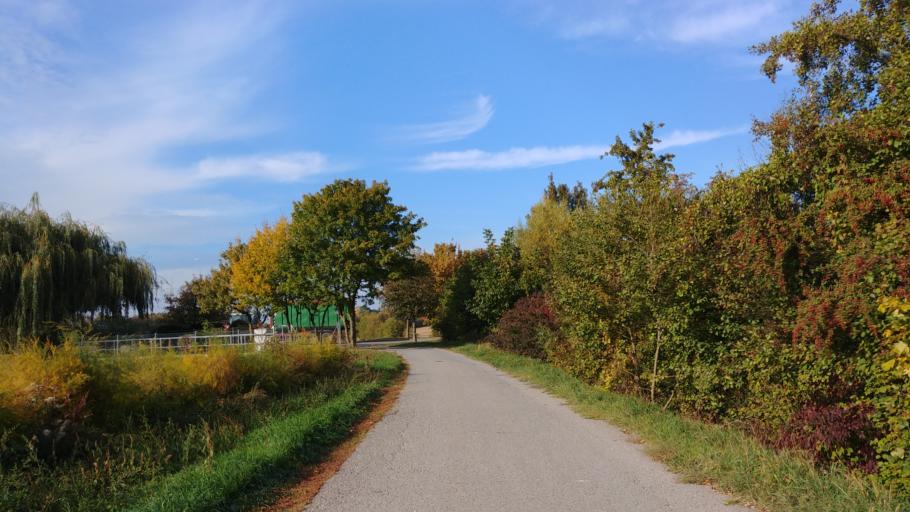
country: DE
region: Baden-Wuerttemberg
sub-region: Regierungsbezirk Stuttgart
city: Abstatt
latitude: 49.0588
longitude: 9.2750
